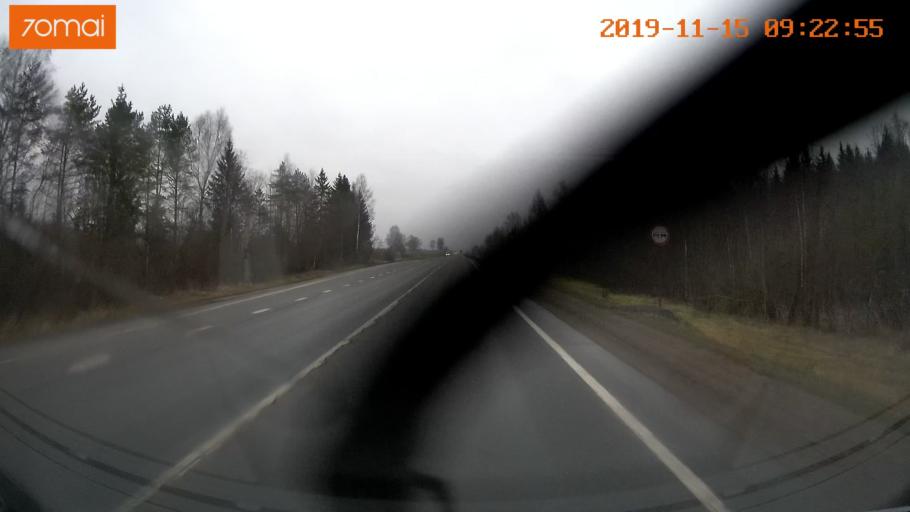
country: RU
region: Vologda
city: Tonshalovo
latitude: 59.2993
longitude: 38.1004
